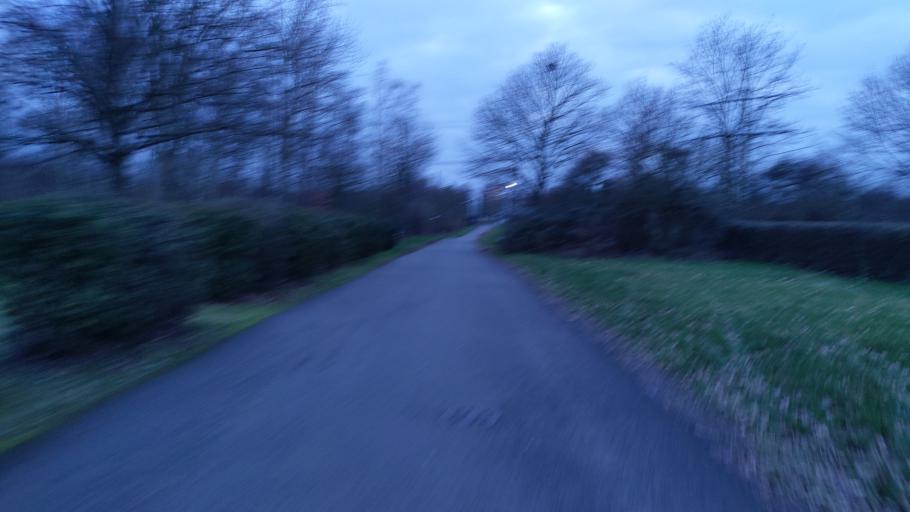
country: DE
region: North Rhine-Westphalia
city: Monheim am Rhein
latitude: 51.0333
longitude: 6.9000
